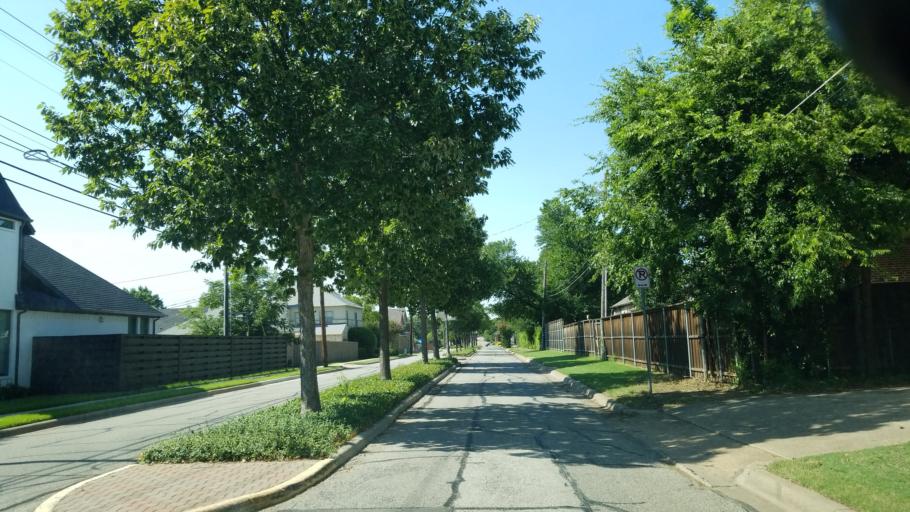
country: US
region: Texas
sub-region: Dallas County
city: Farmers Branch
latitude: 32.9220
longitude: -96.8874
